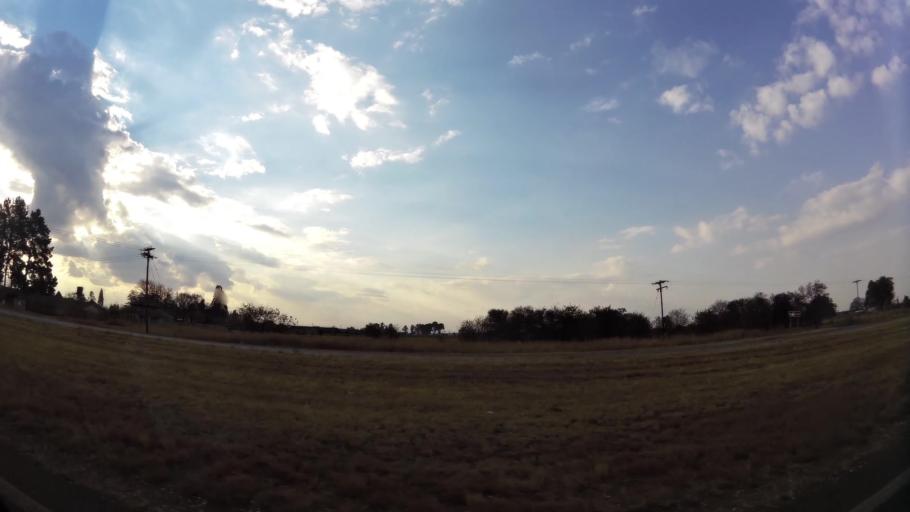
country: ZA
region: Gauteng
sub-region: Sedibeng District Municipality
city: Vanderbijlpark
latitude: -26.6195
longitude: 27.8189
